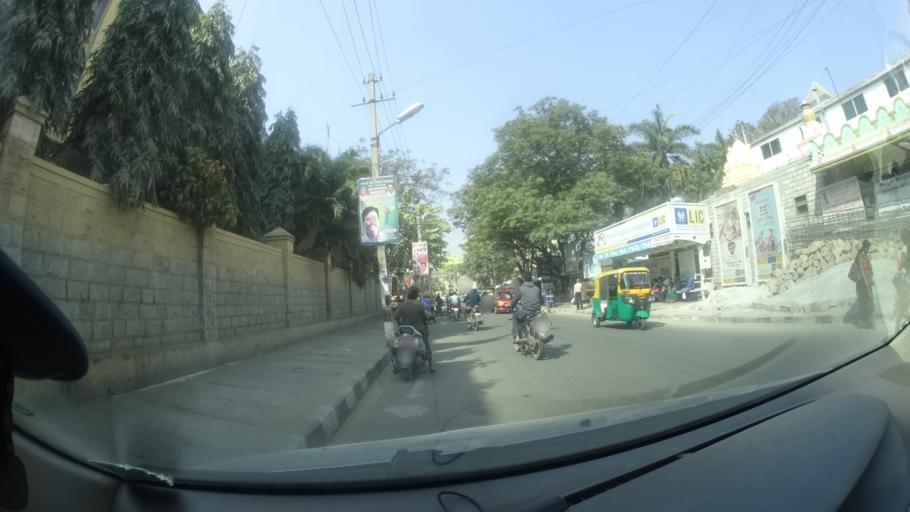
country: IN
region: Karnataka
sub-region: Bangalore Urban
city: Bangalore
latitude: 12.9990
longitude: 77.5747
